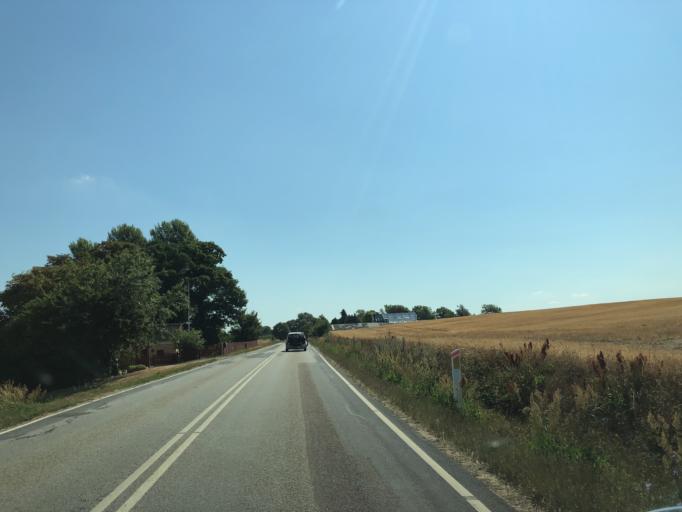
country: DK
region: Zealand
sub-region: Odsherred Kommune
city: Hojby
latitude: 55.9383
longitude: 11.5706
